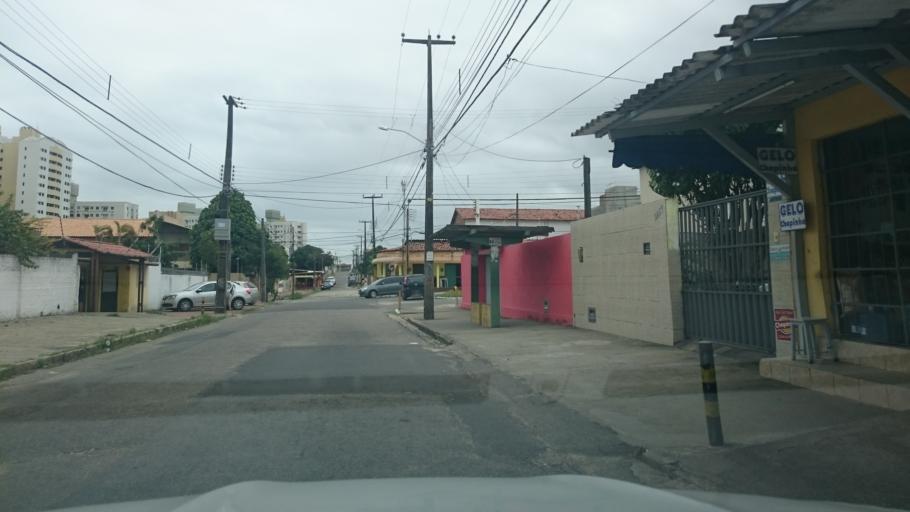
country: BR
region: Rio Grande do Norte
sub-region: Parnamirim
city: Parnamirim
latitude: -5.8742
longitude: -35.2126
